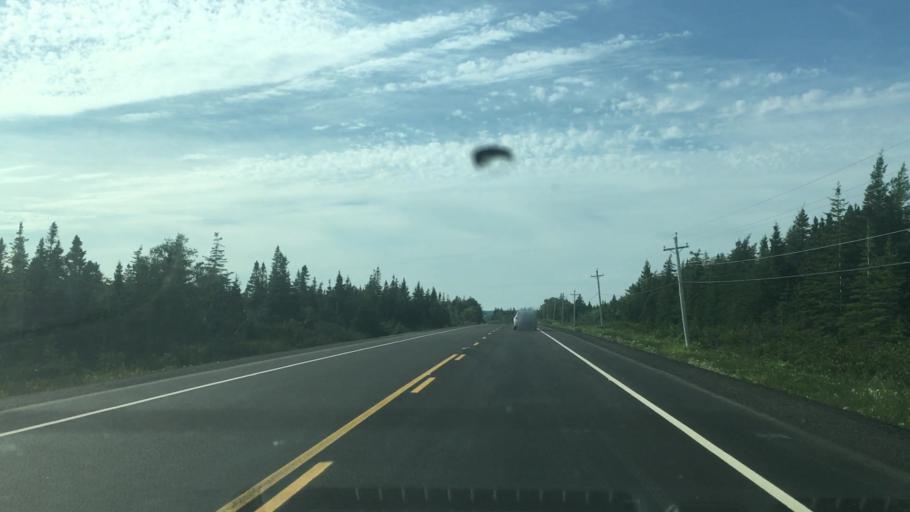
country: CA
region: Nova Scotia
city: Sydney Mines
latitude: 46.8466
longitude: -60.4119
